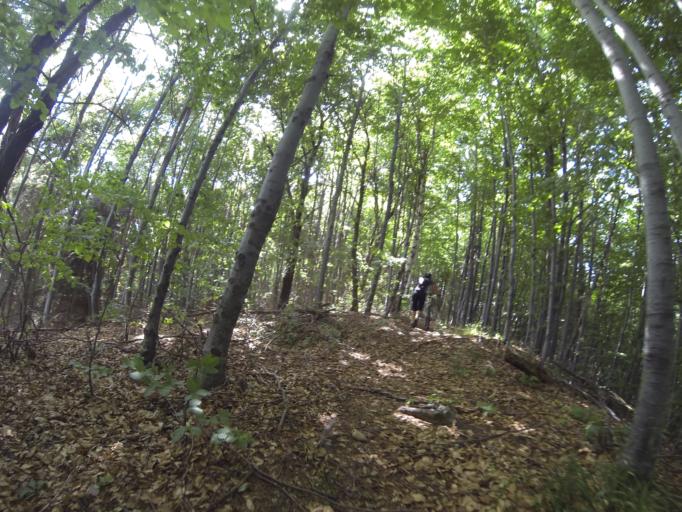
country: RO
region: Valcea
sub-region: Oras Baile Olanesti
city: Cheia
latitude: 45.2423
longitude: 24.1684
